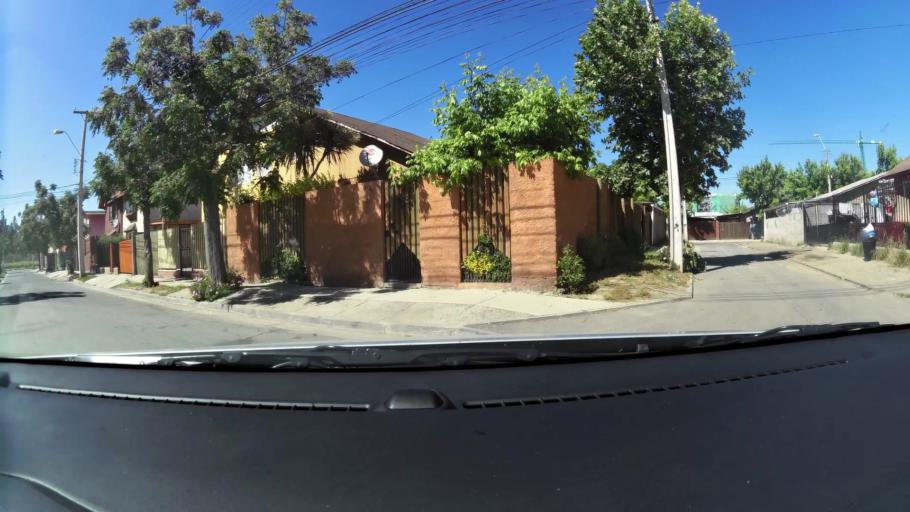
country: CL
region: Valparaiso
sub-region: Provincia de Marga Marga
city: Quilpue
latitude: -33.3090
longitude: -71.4138
